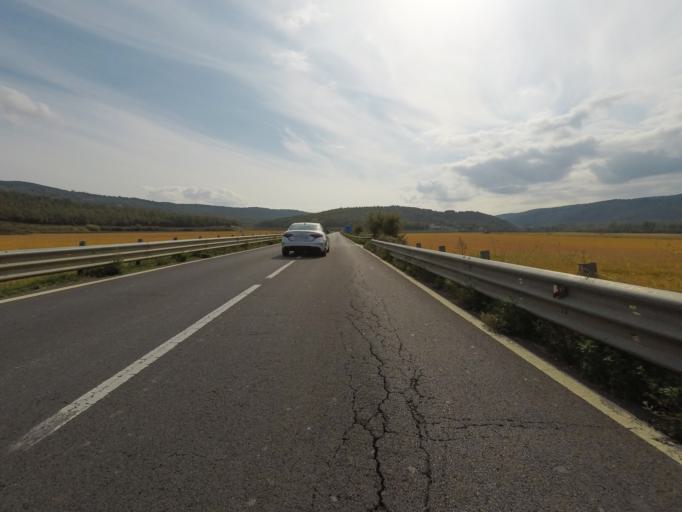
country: IT
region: Tuscany
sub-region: Provincia di Siena
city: Murlo
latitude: 43.1615
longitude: 11.2887
